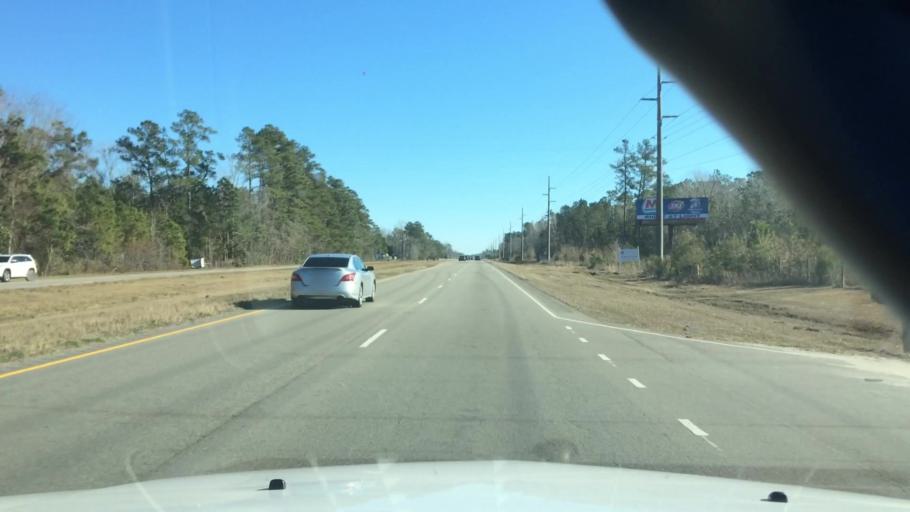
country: US
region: North Carolina
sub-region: Brunswick County
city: Shallotte
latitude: 34.0020
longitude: -78.3163
